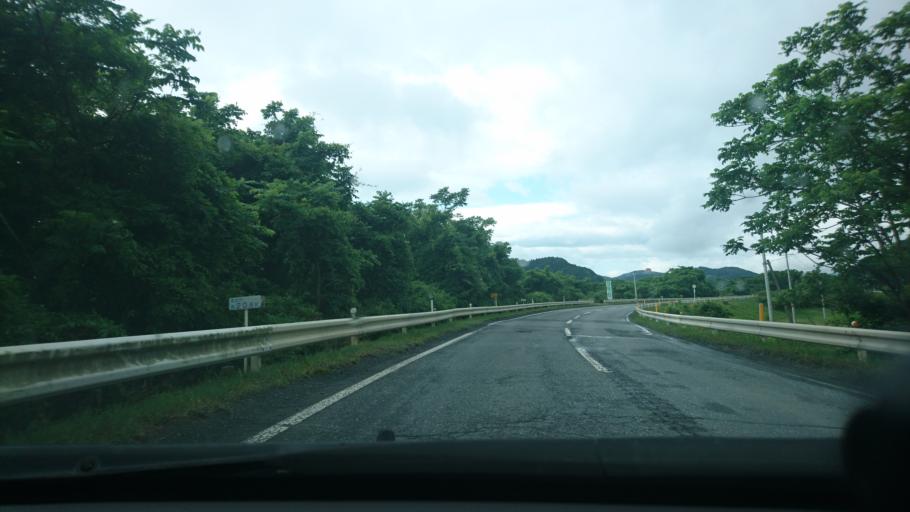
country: JP
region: Miyagi
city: Ishinomaki
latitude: 38.5622
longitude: 141.2997
